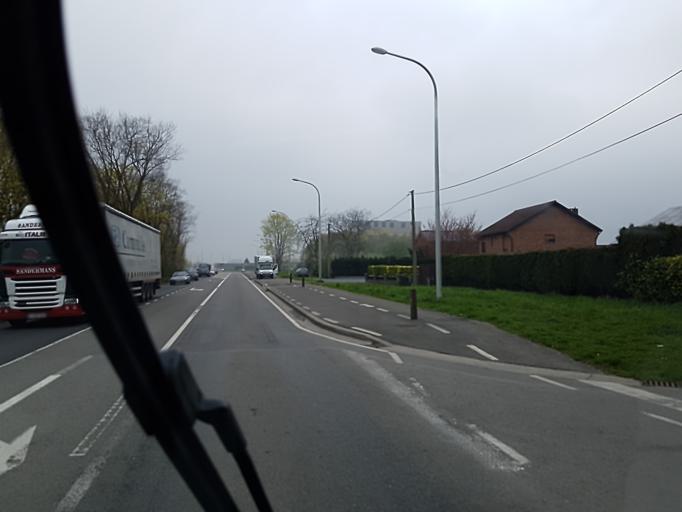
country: BE
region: Wallonia
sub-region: Province du Hainaut
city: Jurbise
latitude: 50.4807
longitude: 3.9059
